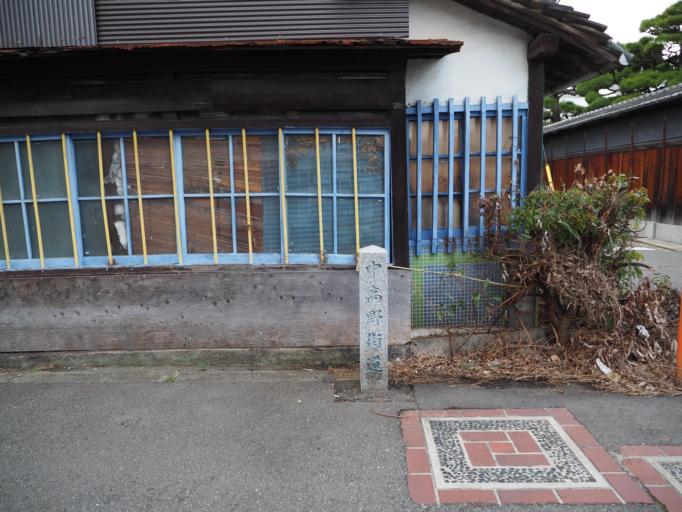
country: JP
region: Osaka
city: Yao
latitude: 34.6128
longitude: 135.5549
